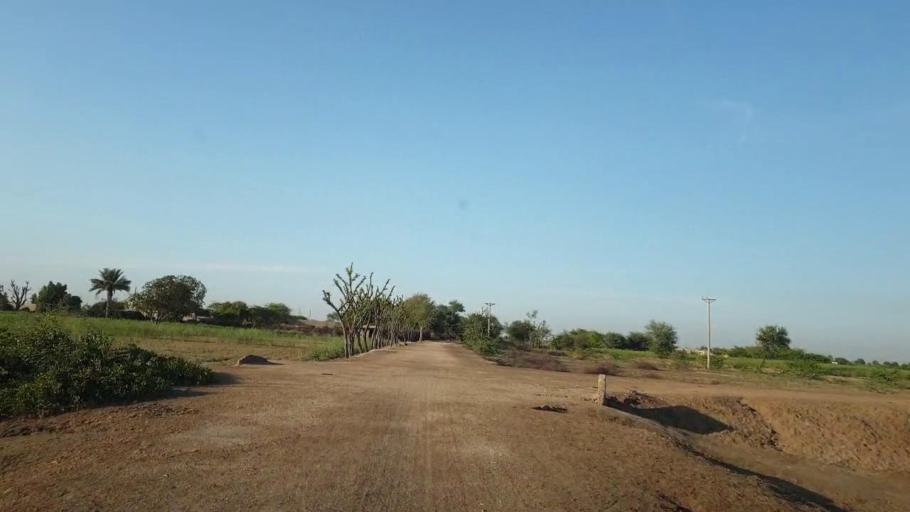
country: PK
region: Sindh
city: Kunri
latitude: 25.0917
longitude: 69.4343
